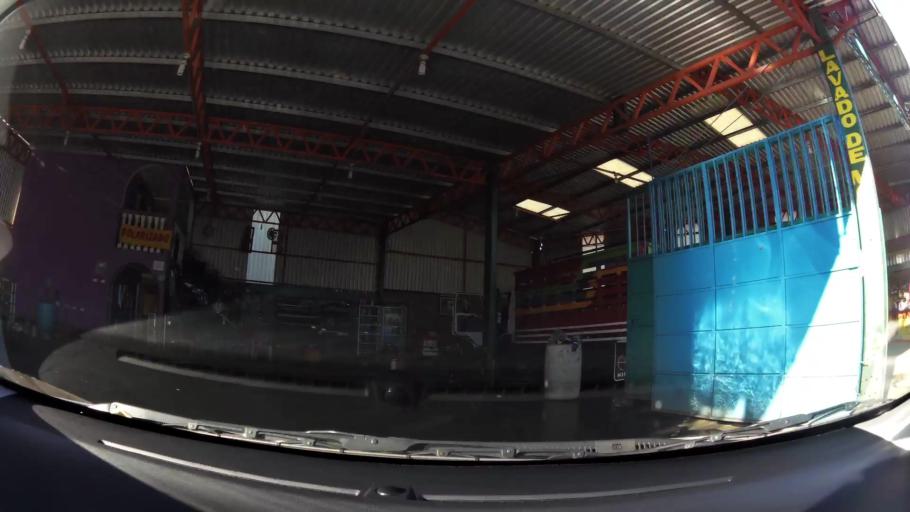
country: SV
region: Sonsonate
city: San Antonio del Monte
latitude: 13.7199
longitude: -89.7328
